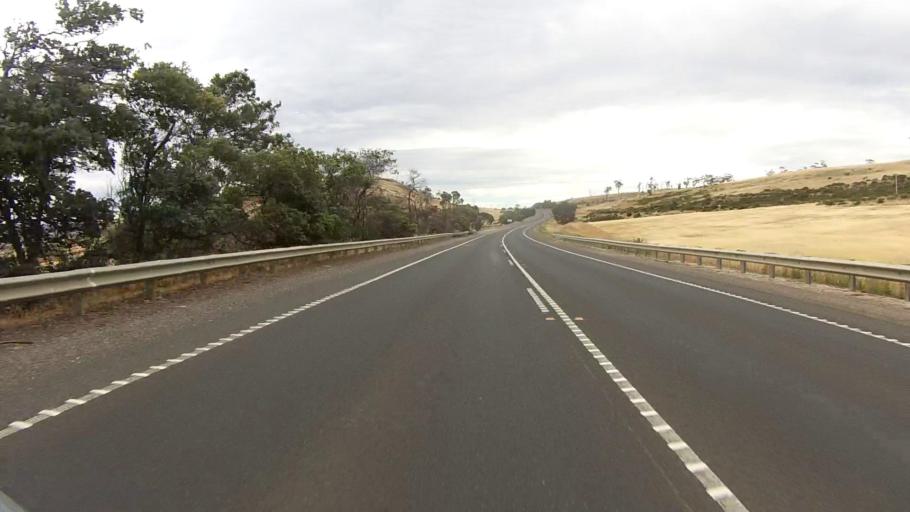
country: AU
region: Tasmania
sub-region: Brighton
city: Bridgewater
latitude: -42.3440
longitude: 147.3387
